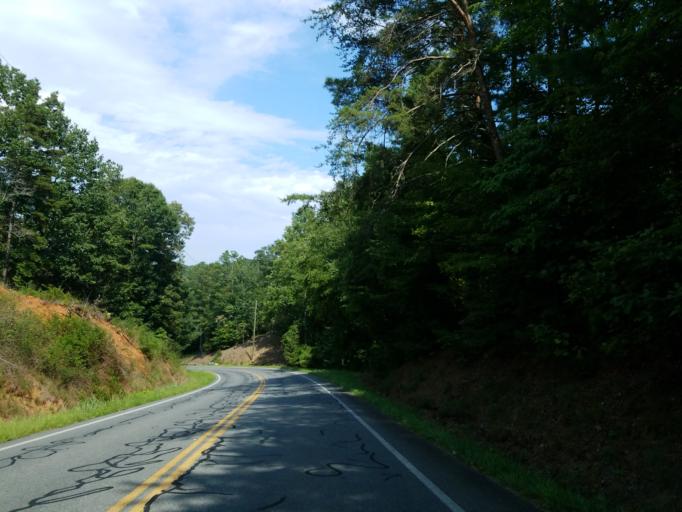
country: US
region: Georgia
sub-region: Gilmer County
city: Ellijay
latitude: 34.5819
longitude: -84.6049
